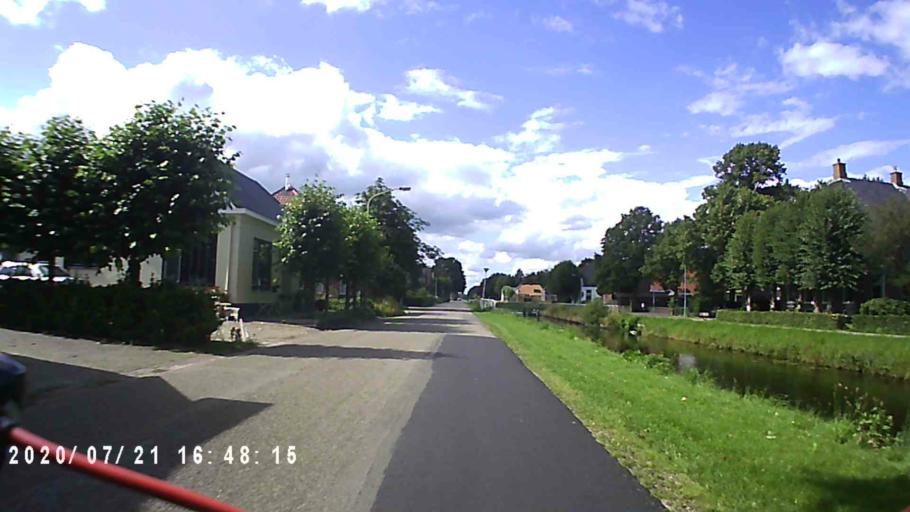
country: NL
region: Groningen
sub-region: Gemeente Hoogezand-Sappemeer
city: Hoogezand
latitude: 53.1161
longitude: 6.7764
